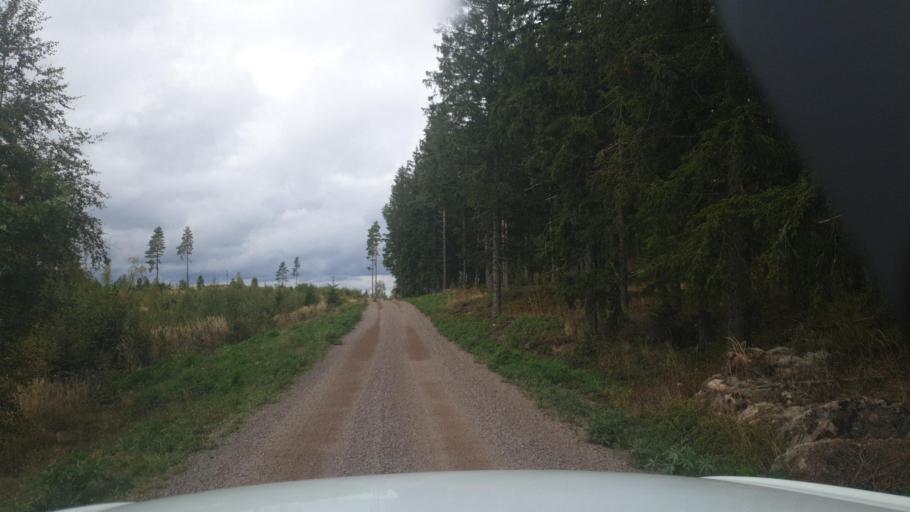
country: SE
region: Vaermland
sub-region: Torsby Kommun
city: Torsby
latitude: 59.9529
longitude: 12.7787
